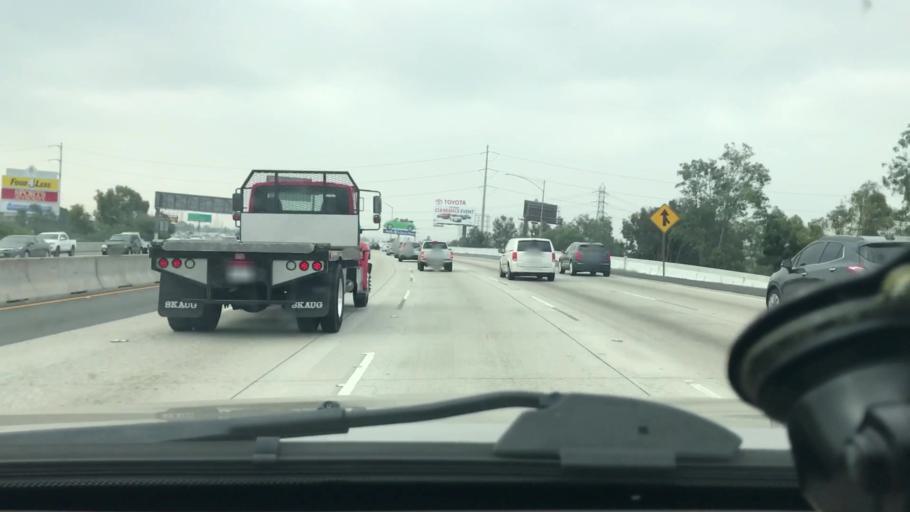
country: US
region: California
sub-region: Los Angeles County
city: Del Aire
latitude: 33.8995
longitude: -118.3695
